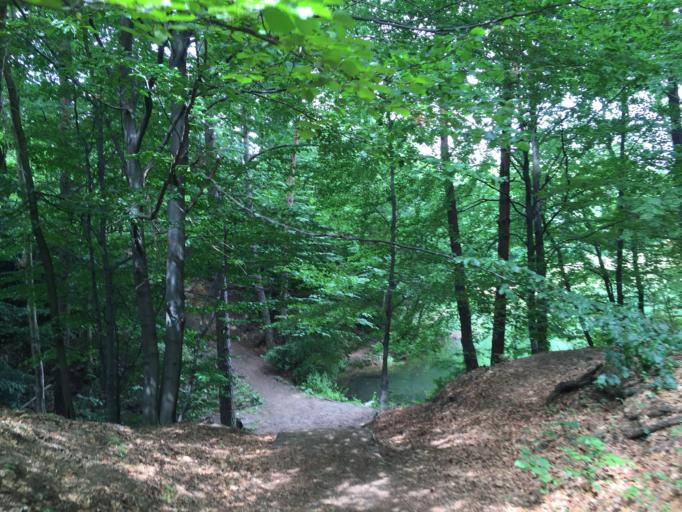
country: PL
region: Lesser Poland Voivodeship
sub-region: Powiat olkuski
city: Klucze
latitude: 50.3413
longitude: 19.5499
